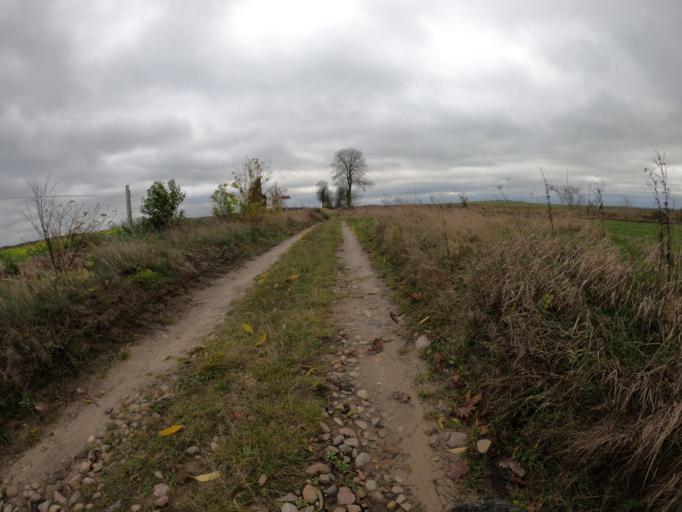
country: PL
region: West Pomeranian Voivodeship
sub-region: Powiat walecki
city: Tuczno
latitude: 53.2495
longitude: 16.2040
